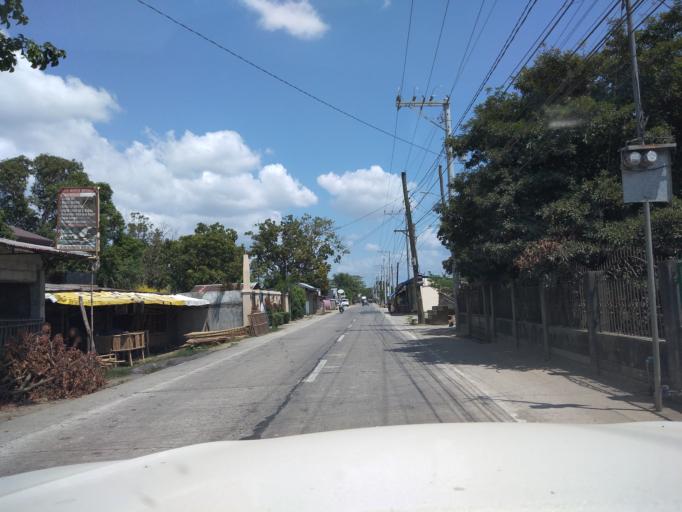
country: PH
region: Central Luzon
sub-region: Province of Pampanga
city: Bahay Pare
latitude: 15.0167
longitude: 120.8773
